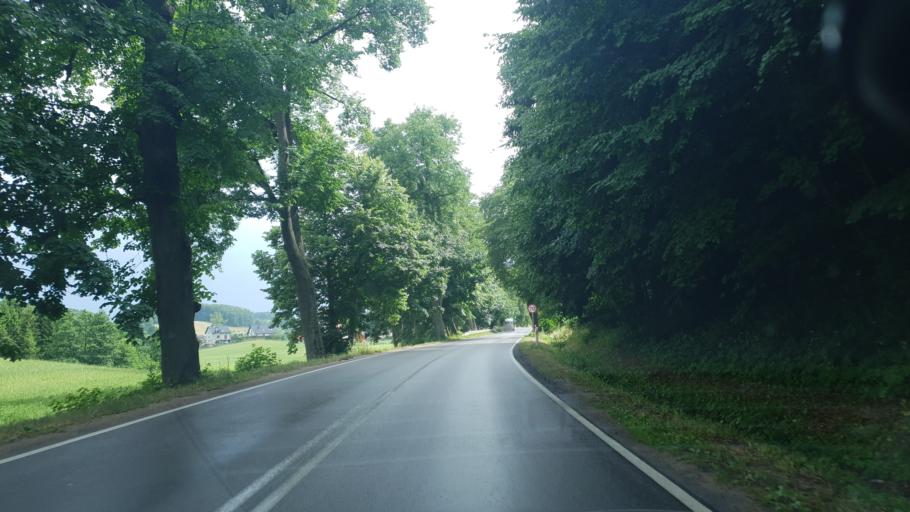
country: PL
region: Pomeranian Voivodeship
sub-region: Powiat kartuski
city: Chmielno
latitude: 54.3078
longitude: 18.1498
